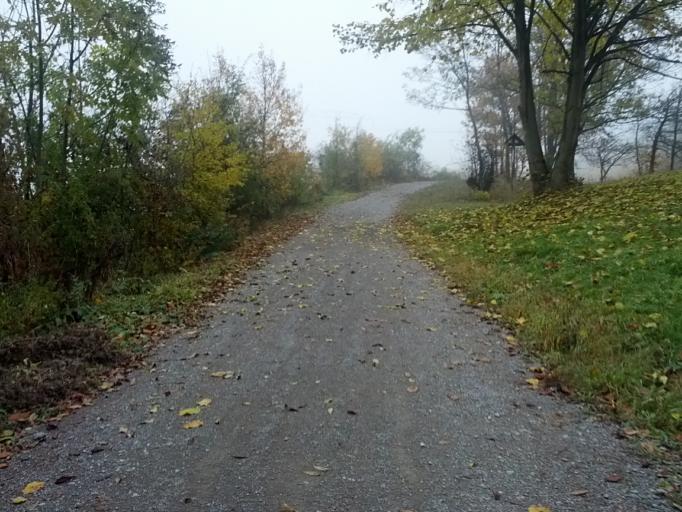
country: DE
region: Thuringia
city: Eisenach
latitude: 50.9697
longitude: 10.3652
